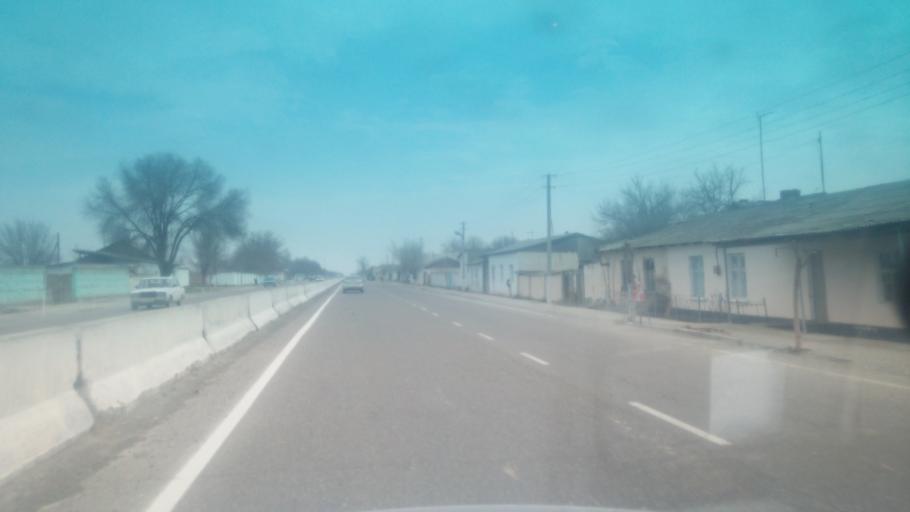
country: KZ
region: Ongtustik Qazaqstan
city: Myrzakent
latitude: 40.5002
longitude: 68.5609
